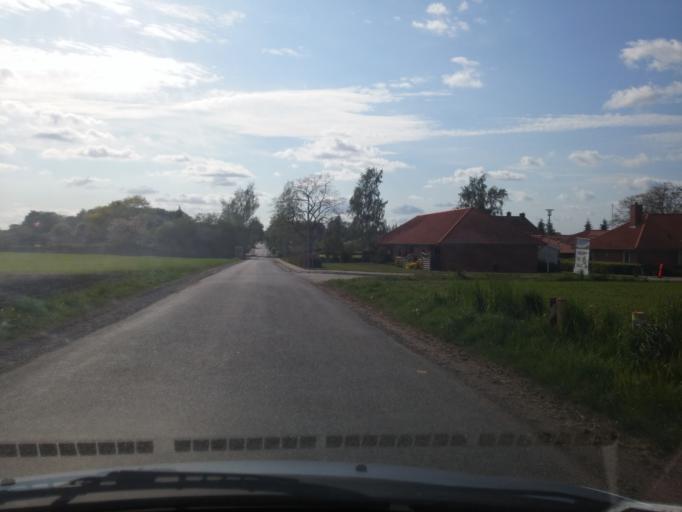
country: DK
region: South Denmark
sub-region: Kerteminde Kommune
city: Langeskov
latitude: 55.3963
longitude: 10.6113
